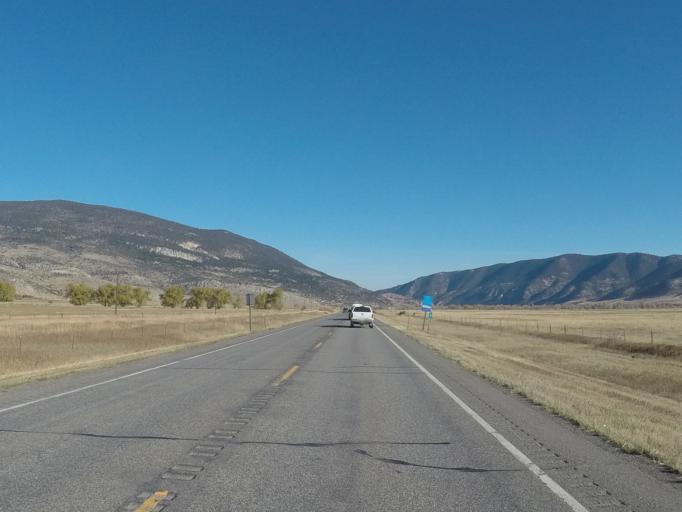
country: US
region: Montana
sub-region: Park County
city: Livingston
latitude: 45.5475
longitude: -110.5985
